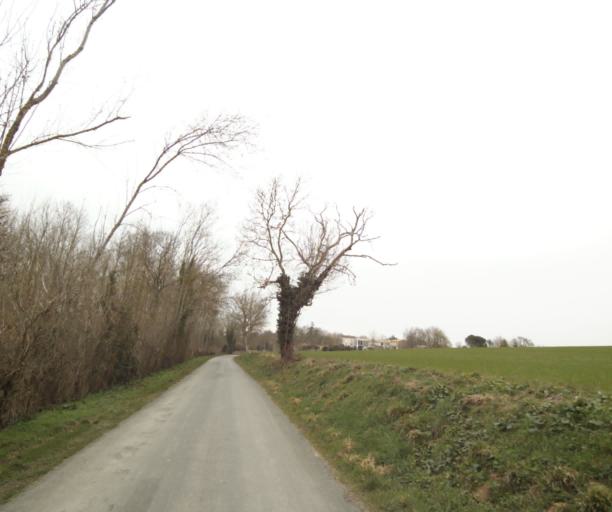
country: FR
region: Poitou-Charentes
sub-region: Departement des Deux-Sevres
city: Magne
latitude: 46.3210
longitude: -0.5328
